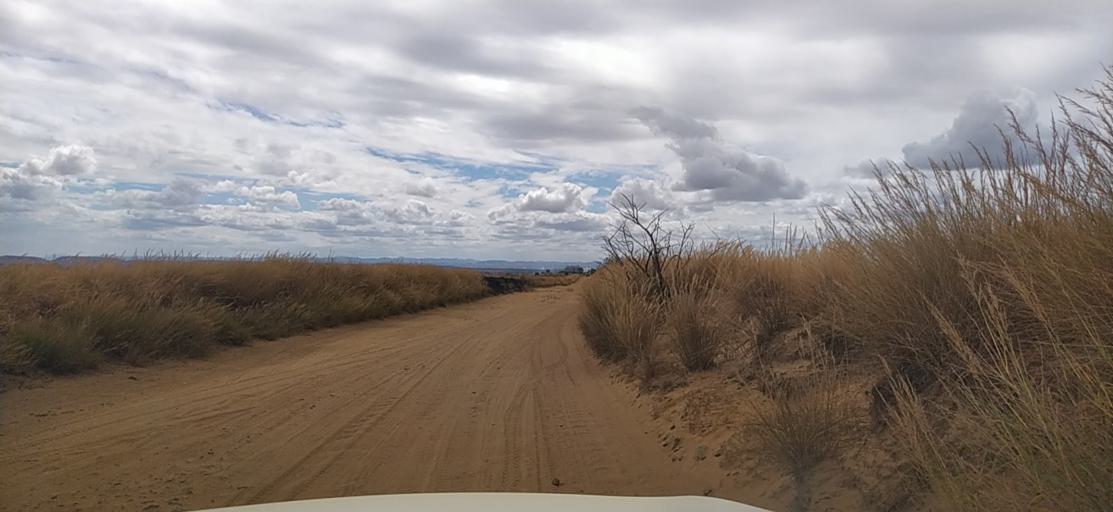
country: MG
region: Alaotra Mangoro
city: Ambatondrazaka
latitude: -17.9113
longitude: 48.2648
